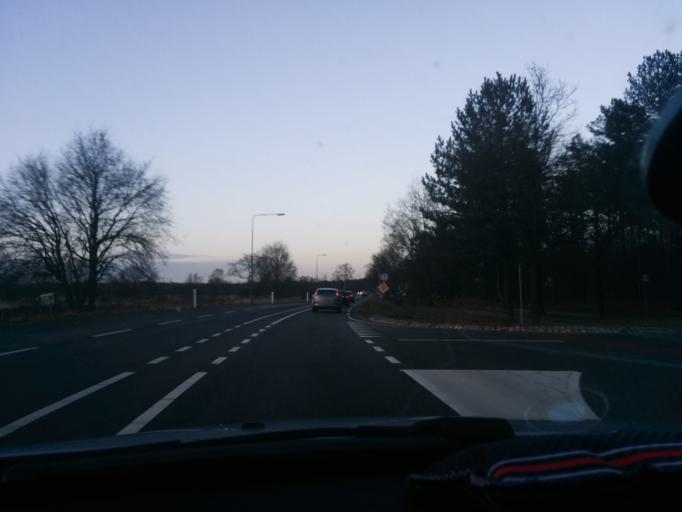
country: NL
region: Utrecht
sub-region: Gemeente Utrechtse Heuvelrug
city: Maarn
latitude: 52.1118
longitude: 5.3602
